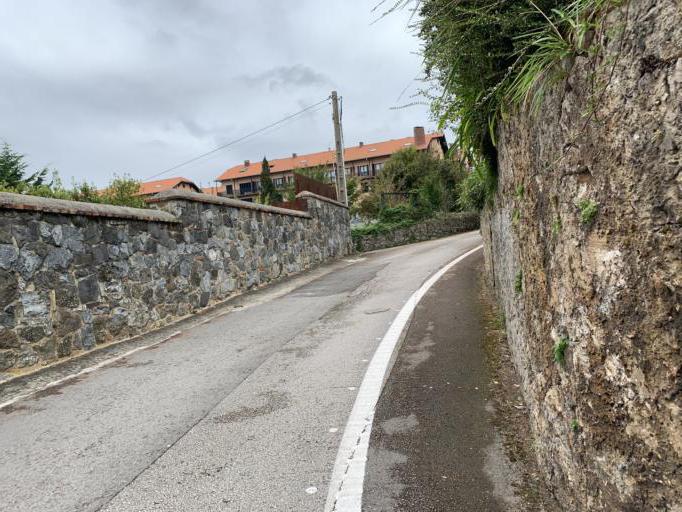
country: ES
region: Cantabria
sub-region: Provincia de Cantabria
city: Comillas
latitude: 43.3868
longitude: -4.2851
